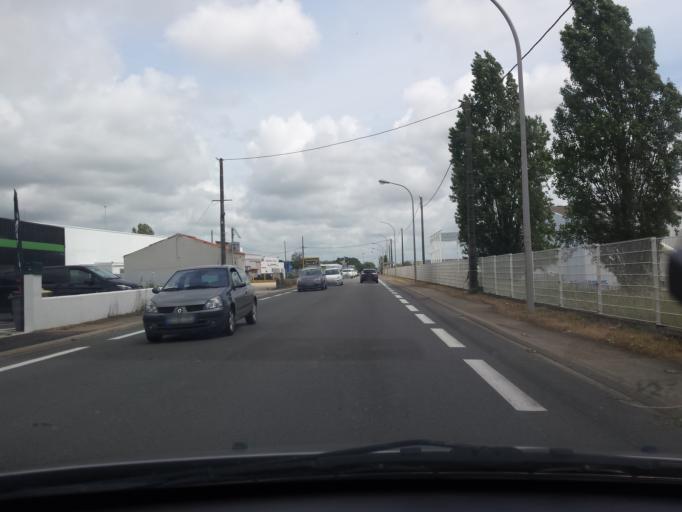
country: FR
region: Pays de la Loire
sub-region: Departement de la Vendee
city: Le Fenouiller
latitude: 46.6939
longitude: -1.9054
